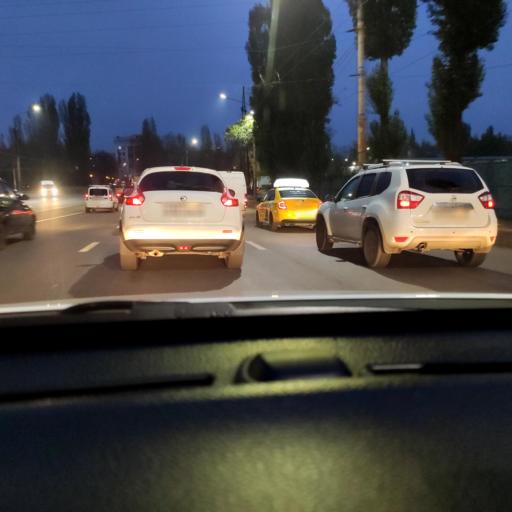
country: RU
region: Voronezj
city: Voronezh
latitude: 51.6327
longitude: 39.2276
